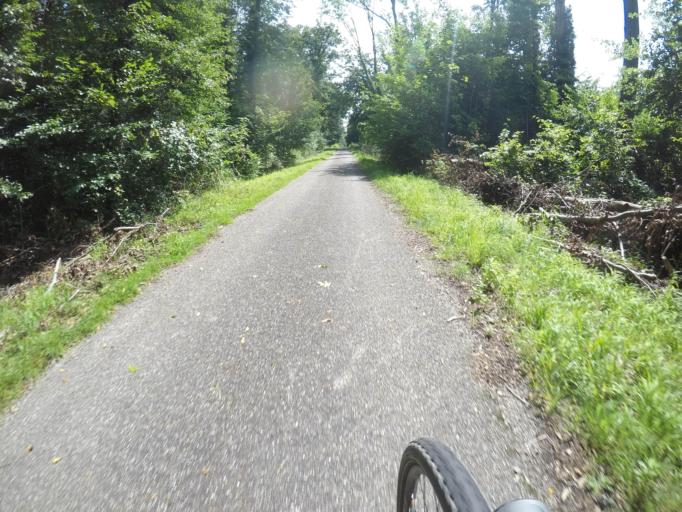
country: DE
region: Baden-Wuerttemberg
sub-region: Karlsruhe Region
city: Kronau
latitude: 49.2139
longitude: 8.5857
